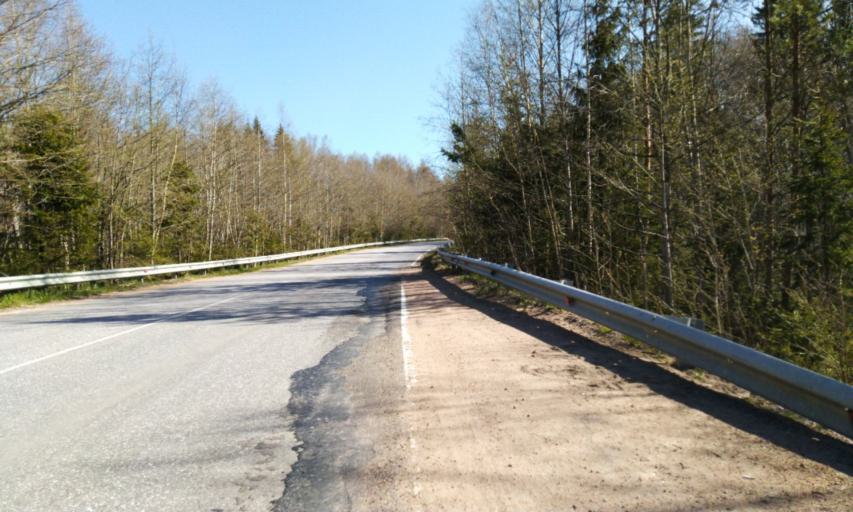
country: RU
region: Leningrad
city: Garbolovo
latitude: 60.3713
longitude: 30.4424
